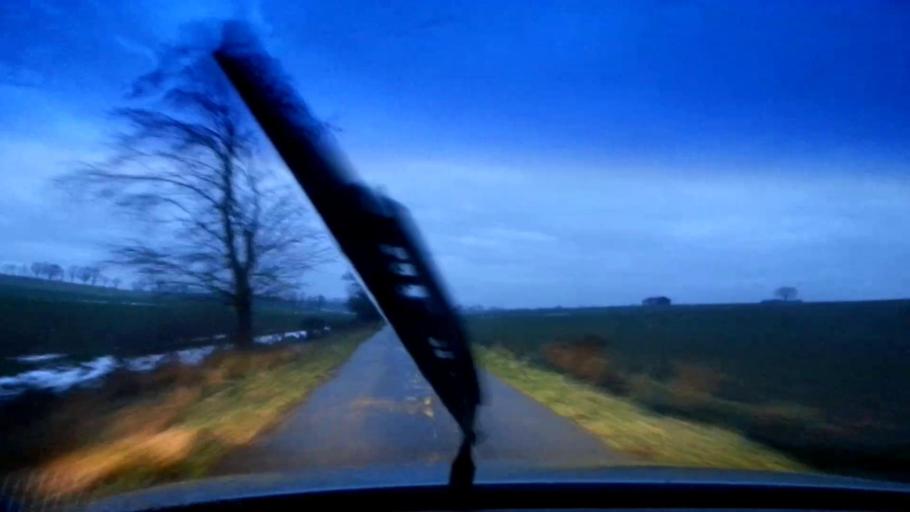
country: DE
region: Bavaria
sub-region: Upper Franconia
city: Memmelsdorf
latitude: 49.9691
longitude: 10.9836
